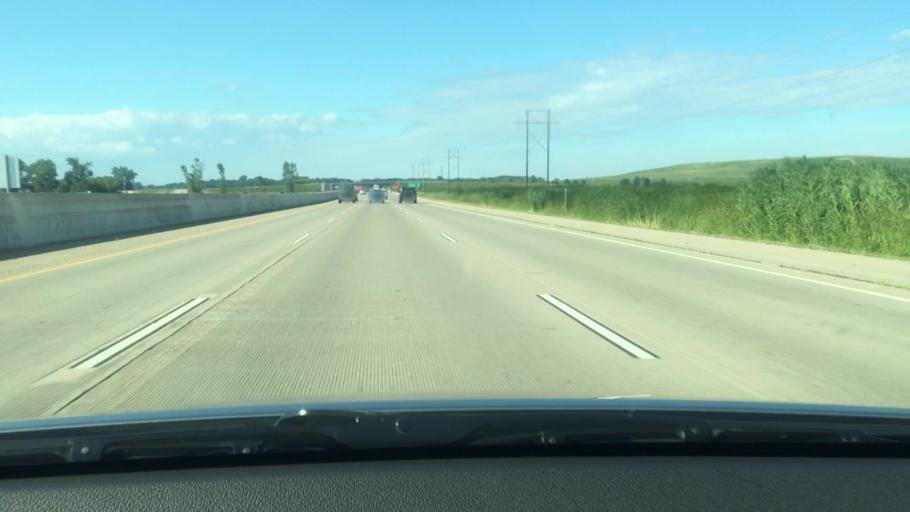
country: US
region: Wisconsin
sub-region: Winnebago County
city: Oshkosh
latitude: 44.0767
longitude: -88.5640
